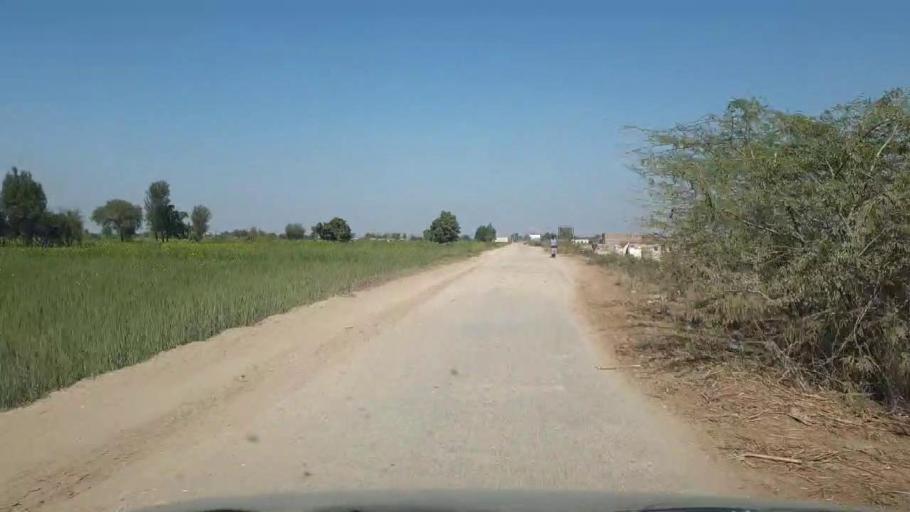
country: PK
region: Sindh
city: Samaro
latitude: 25.2928
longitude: 69.2616
